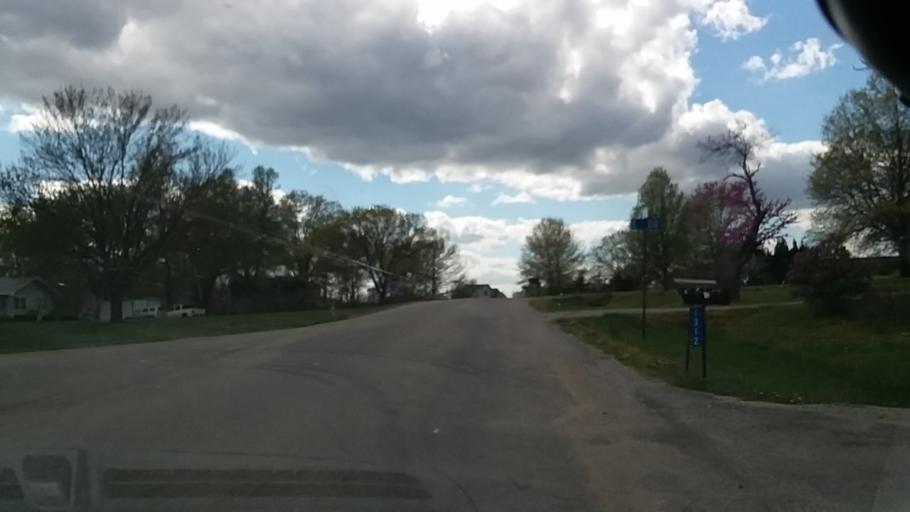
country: US
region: Kansas
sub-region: Douglas County
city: Lawrence
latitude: 38.8927
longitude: -95.2580
